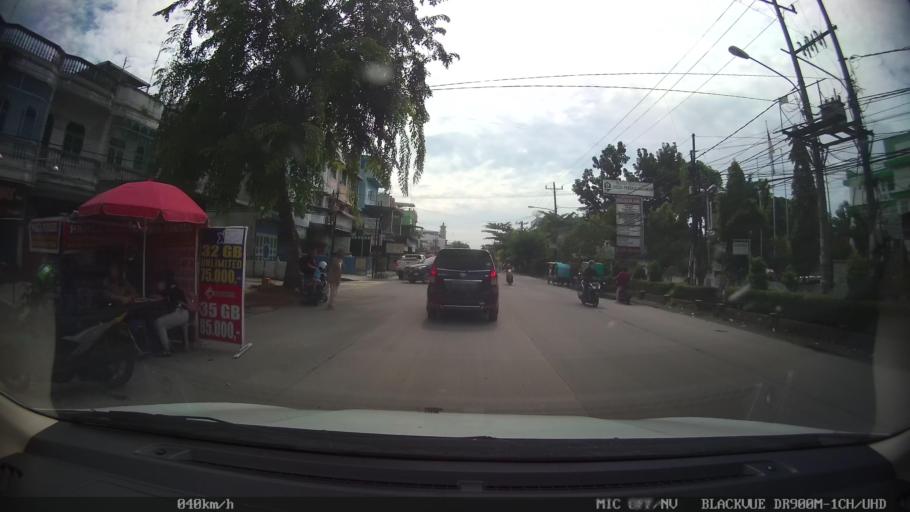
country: ID
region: North Sumatra
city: Medan
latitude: 3.6233
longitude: 98.6747
